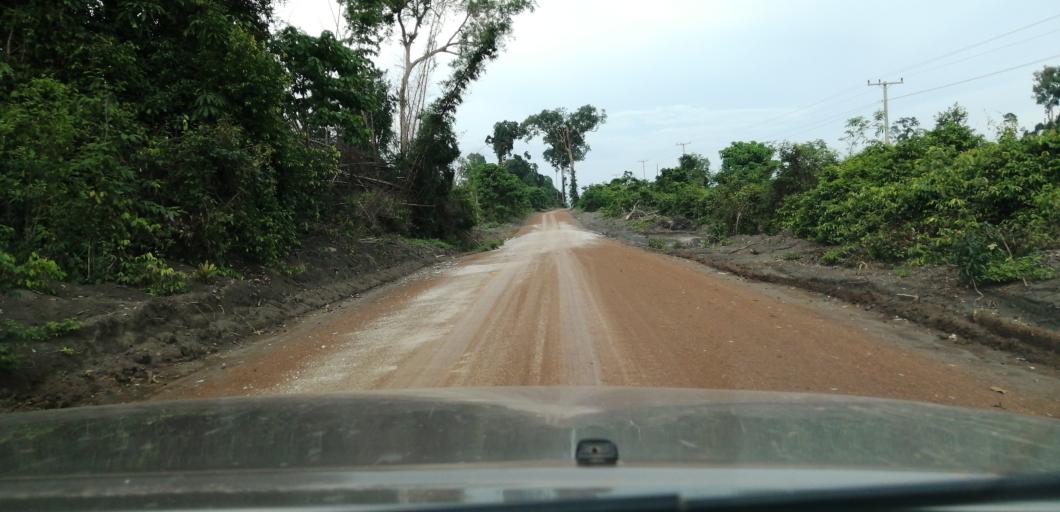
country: LA
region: Champasak
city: Champasak
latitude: 14.7102
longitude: 106.2434
